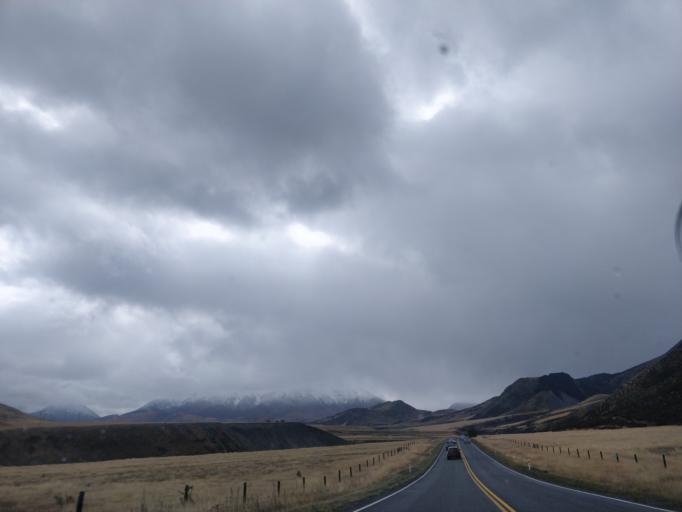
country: NZ
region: Canterbury
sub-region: Ashburton District
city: Methven
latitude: -43.2505
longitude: 171.7171
